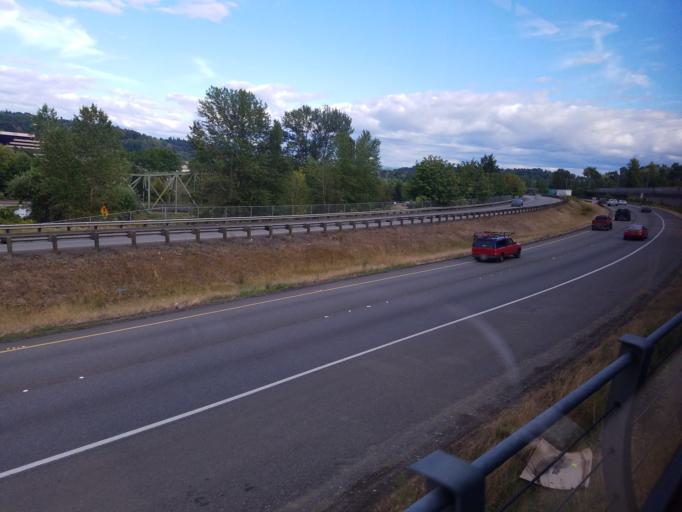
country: US
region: Washington
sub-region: King County
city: Riverton
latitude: 47.4907
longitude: -122.2820
